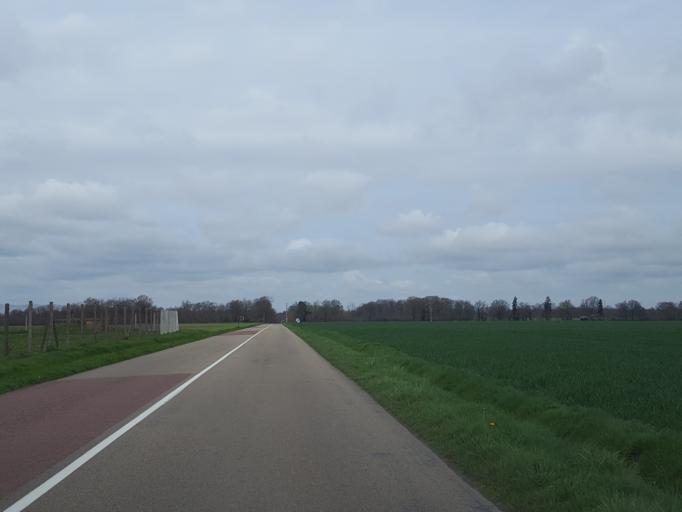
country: FR
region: Centre
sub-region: Departement du Loiret
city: Sainte-Genevieve-des-Bois
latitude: 47.8203
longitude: 2.8305
